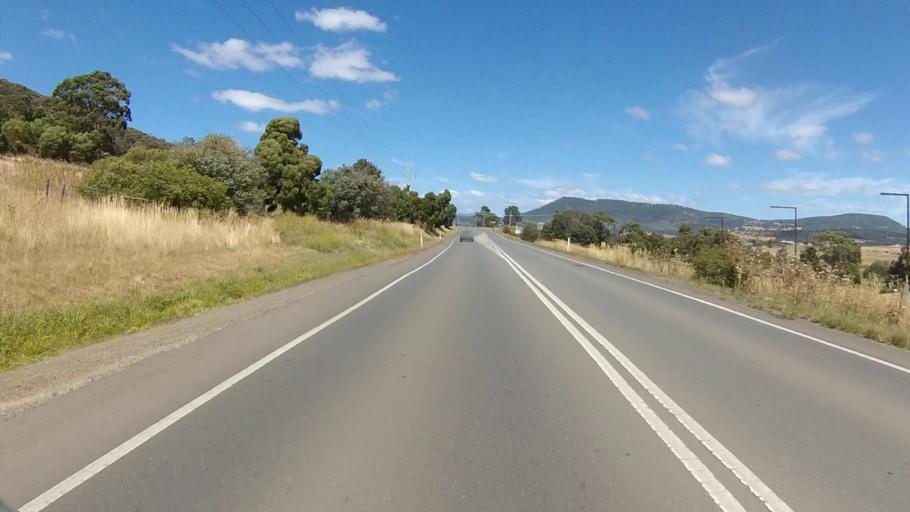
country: AU
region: Tasmania
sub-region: Clarence
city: Cambridge
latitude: -42.7415
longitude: 147.4220
